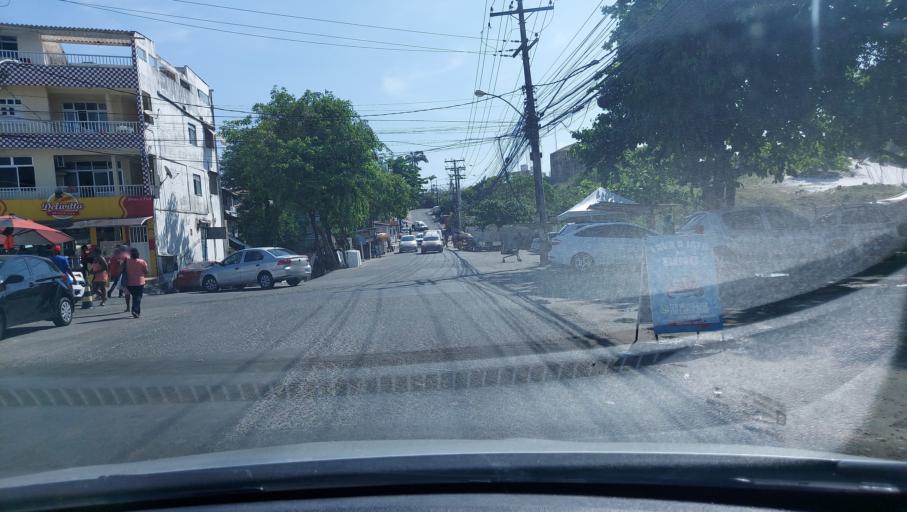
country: BR
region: Bahia
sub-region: Salvador
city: Salvador
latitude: -12.9759
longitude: -38.4368
